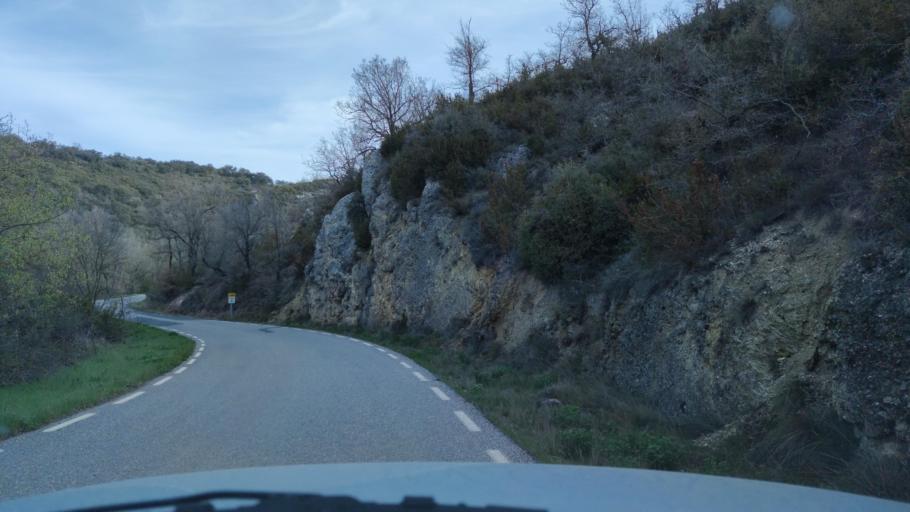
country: ES
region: Catalonia
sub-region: Provincia de Lleida
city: Os de Balaguer
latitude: 41.8857
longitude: 0.7909
